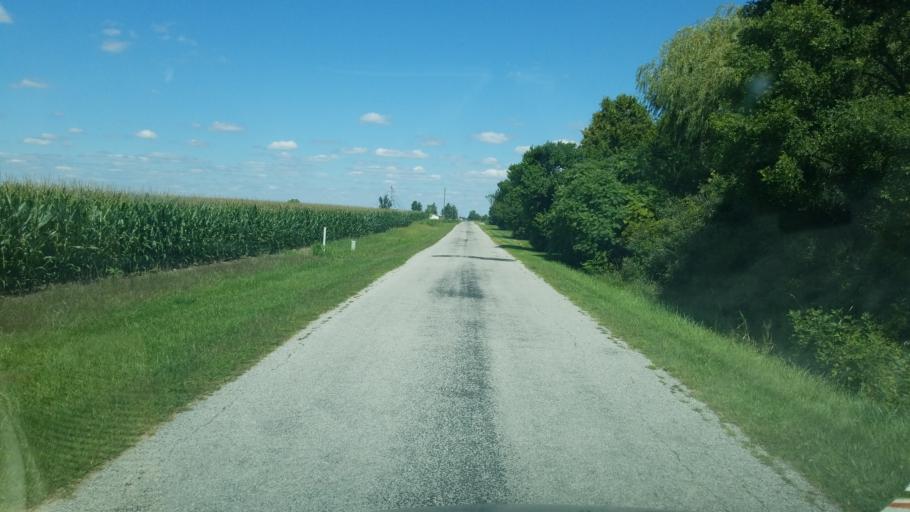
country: US
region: Ohio
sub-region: Fulton County
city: Delta
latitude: 41.6872
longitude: -84.0170
